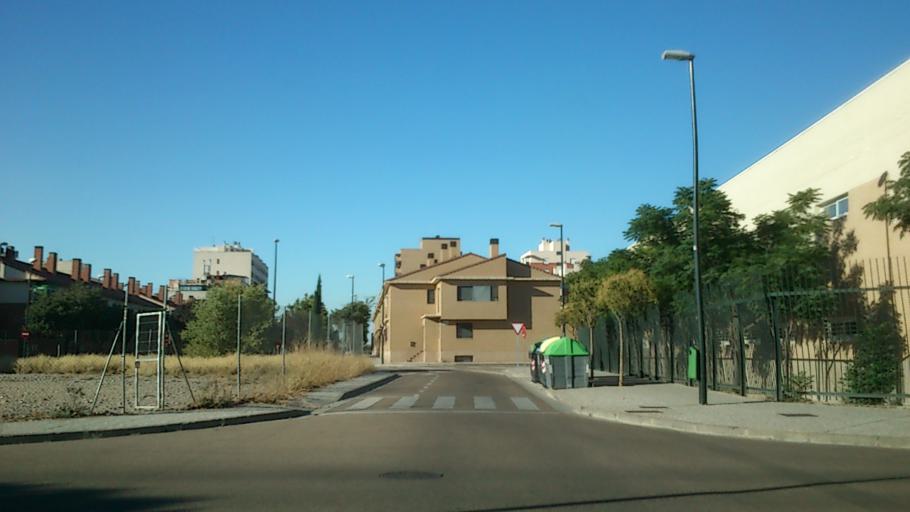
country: ES
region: Aragon
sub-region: Provincia de Zaragoza
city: Zaragoza
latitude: 41.6701
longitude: -0.8324
